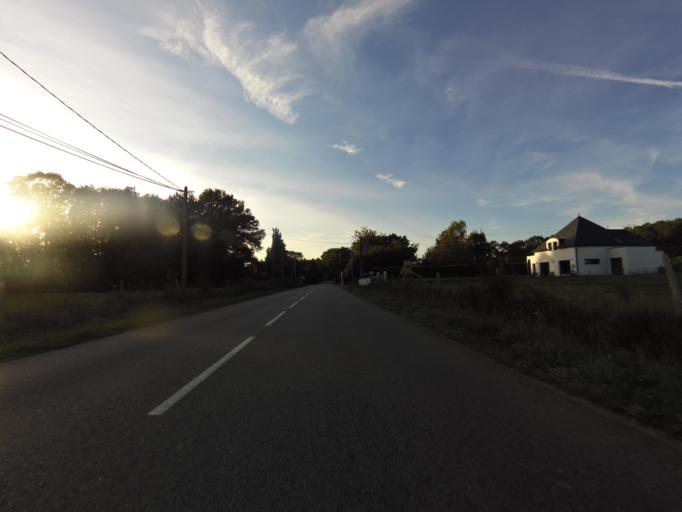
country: FR
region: Brittany
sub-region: Departement du Morbihan
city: Questembert
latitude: 47.6648
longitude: -2.4824
